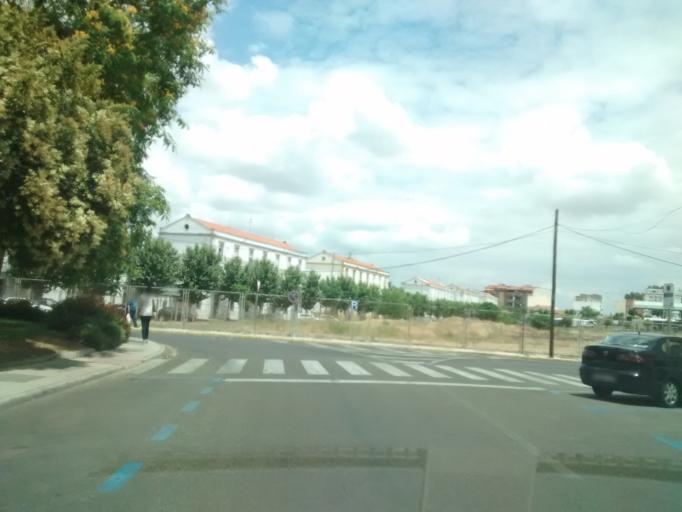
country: ES
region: Extremadura
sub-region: Provincia de Badajoz
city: Merida
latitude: 38.9196
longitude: -6.3397
